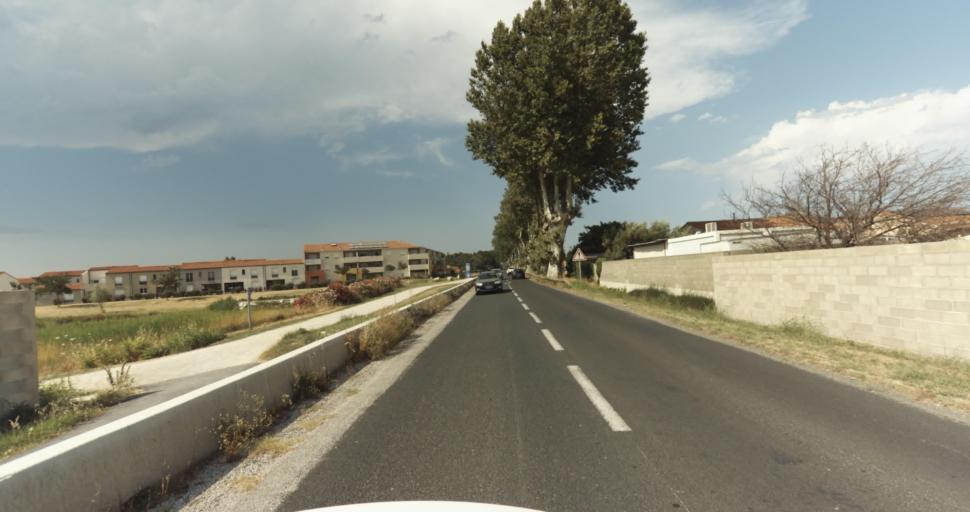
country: FR
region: Languedoc-Roussillon
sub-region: Departement des Pyrenees-Orientales
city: Elne
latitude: 42.6096
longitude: 2.9755
